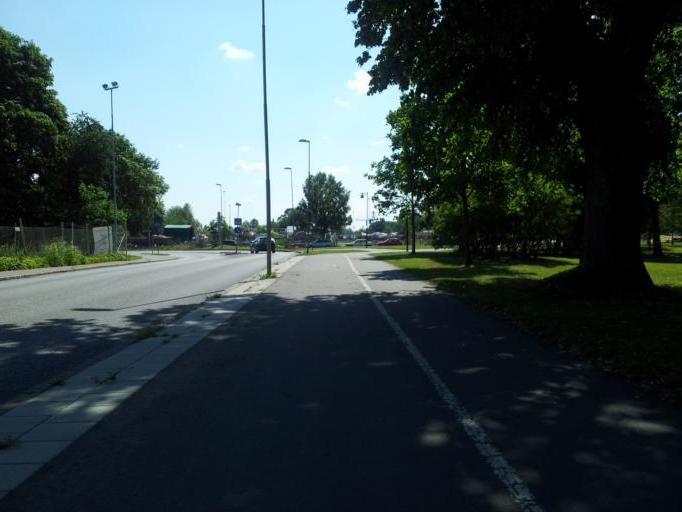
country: SE
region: Uppsala
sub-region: Uppsala Kommun
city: Uppsala
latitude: 59.8473
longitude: 17.6511
